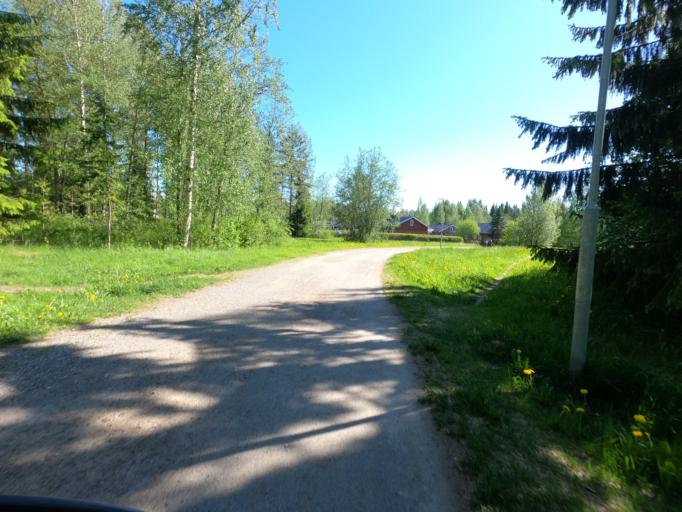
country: FI
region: North Karelia
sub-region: Joensuu
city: Joensuu
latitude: 62.5890
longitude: 29.8002
